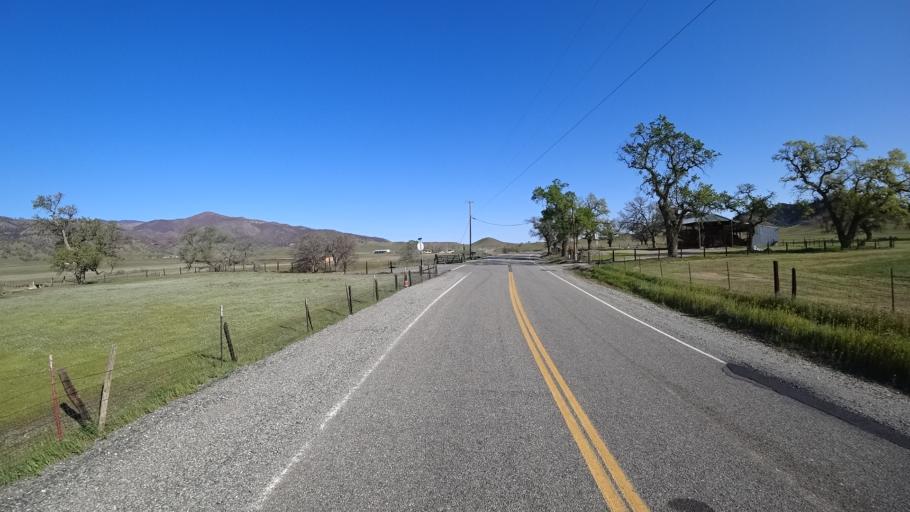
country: US
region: California
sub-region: Tehama County
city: Rancho Tehama Reserve
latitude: 39.6987
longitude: -122.5501
